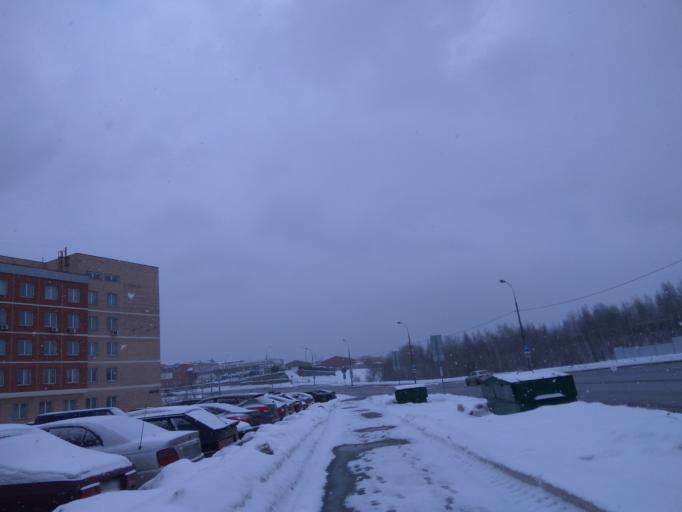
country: RU
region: Moscow
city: Rublevo
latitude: 55.7959
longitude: 37.3823
